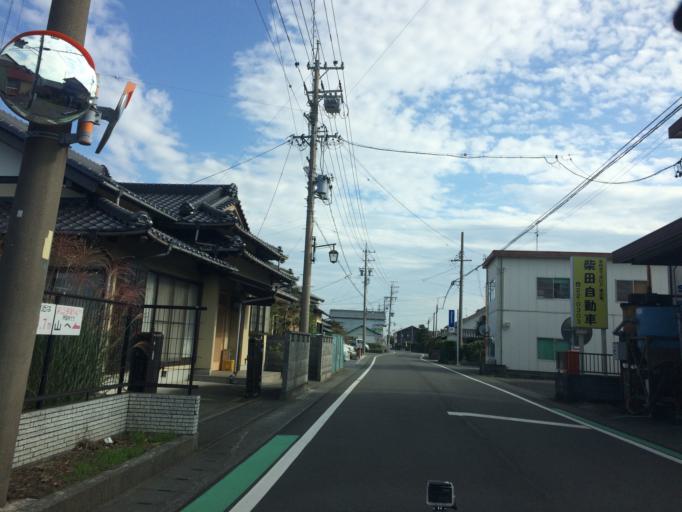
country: JP
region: Shizuoka
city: Sagara
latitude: 34.7514
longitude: 138.2352
